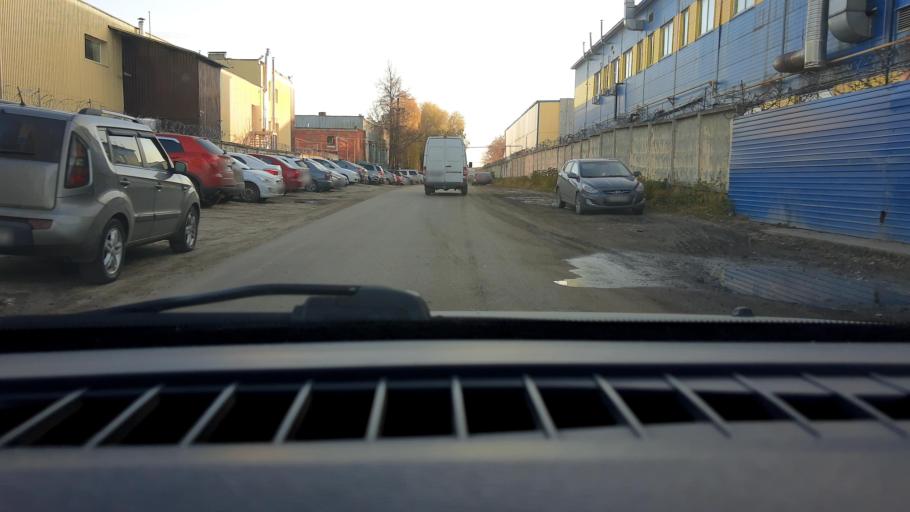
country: RU
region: Nizjnij Novgorod
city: Gorbatovka
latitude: 56.3093
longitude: 43.8656
